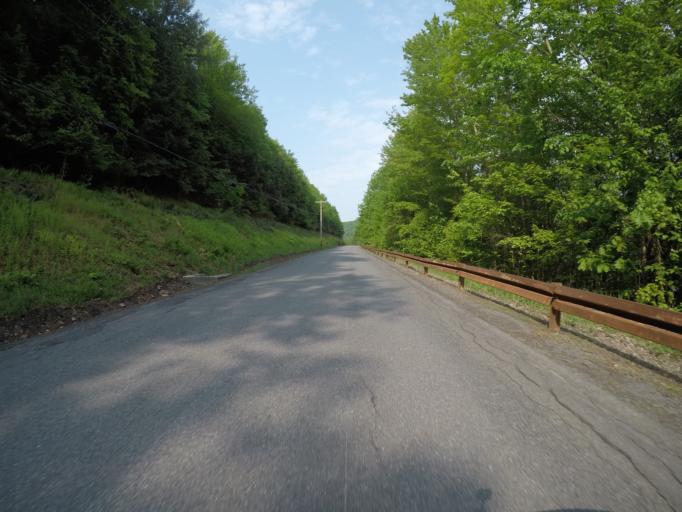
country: US
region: New York
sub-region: Sullivan County
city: Livingston Manor
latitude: 42.0984
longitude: -74.7855
